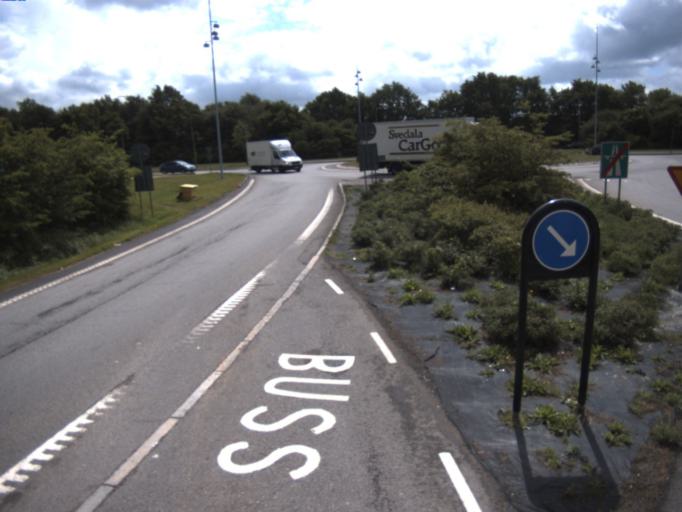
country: SE
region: Skane
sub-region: Helsingborg
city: Rydeback
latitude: 56.0169
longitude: 12.7576
